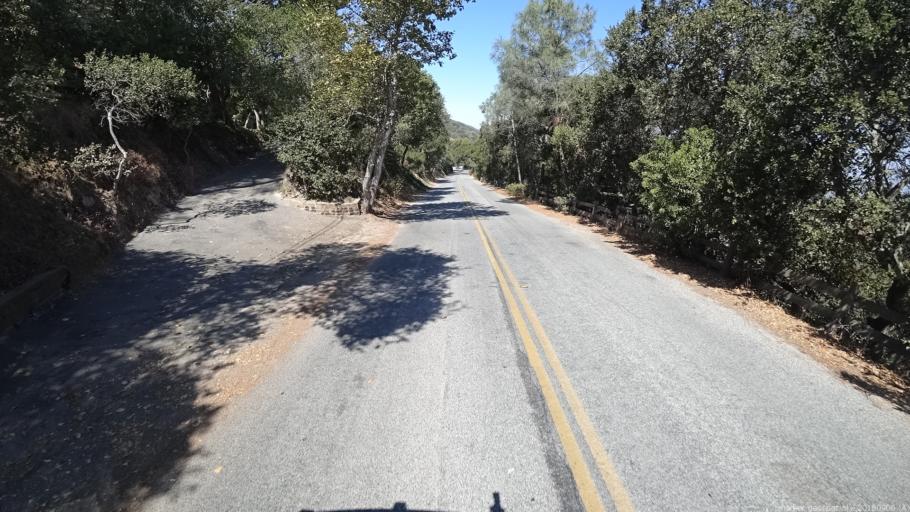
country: US
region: California
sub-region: Monterey County
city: Salinas
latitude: 36.5773
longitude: -121.6293
